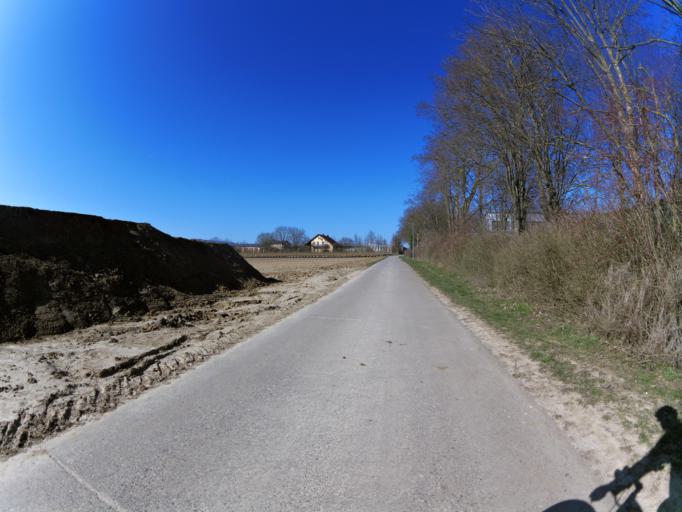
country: DE
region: Bavaria
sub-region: Regierungsbezirk Unterfranken
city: Bergtheim
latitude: 49.8931
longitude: 10.0690
